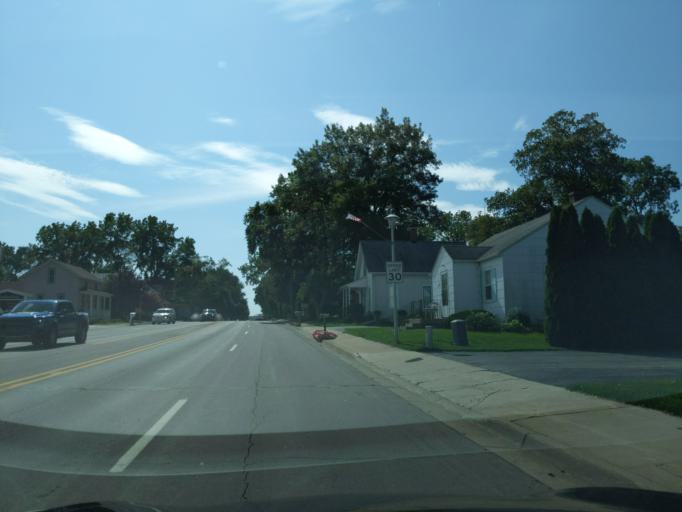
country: US
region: Michigan
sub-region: Saginaw County
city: Frankenmuth
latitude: 43.3215
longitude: -83.7405
